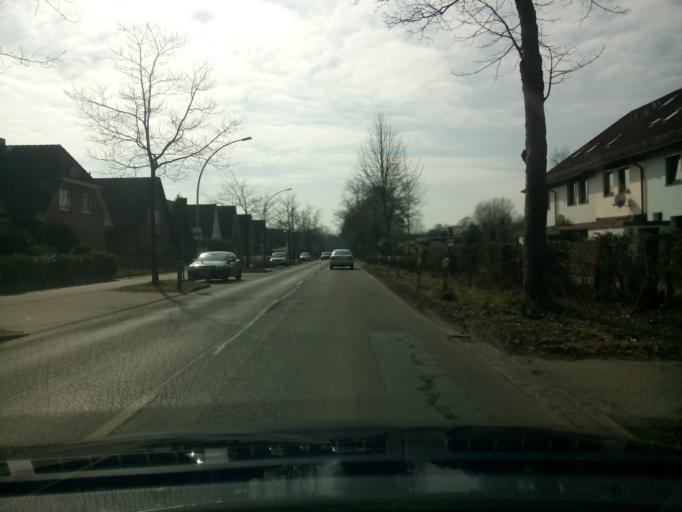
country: DE
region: Lower Saxony
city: Osterholz-Scharmbeck
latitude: 53.2216
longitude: 8.7827
